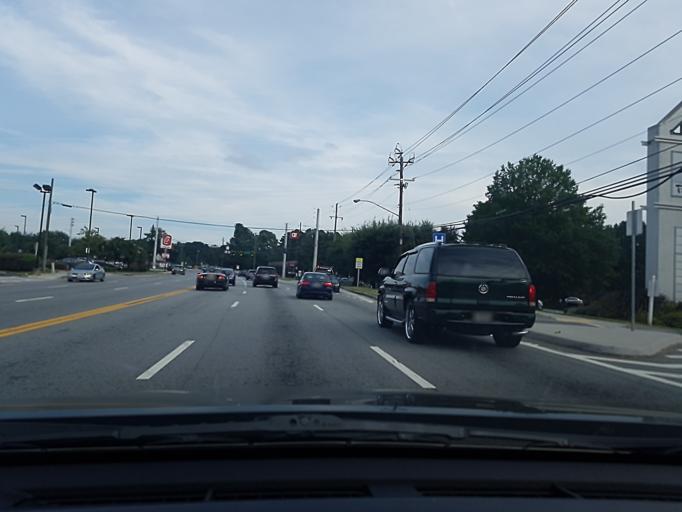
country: US
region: Georgia
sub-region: DeKalb County
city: North Druid Hills
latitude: 33.8283
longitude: -84.3310
